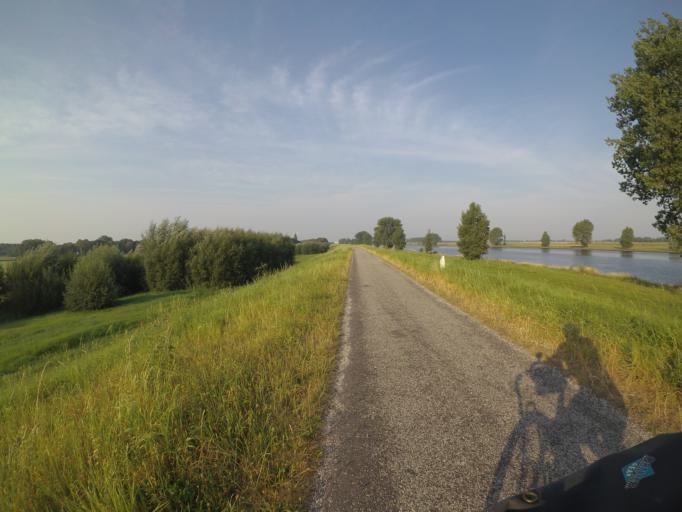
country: NL
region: North Brabant
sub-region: Gemeente Heusden
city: Heusden
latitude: 51.7264
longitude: 5.0929
